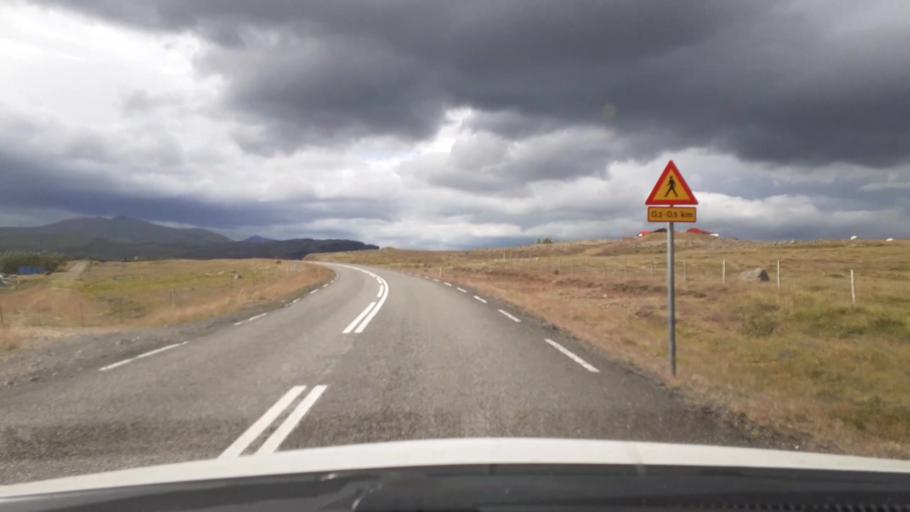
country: IS
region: West
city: Borgarnes
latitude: 64.5464
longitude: -21.6532
